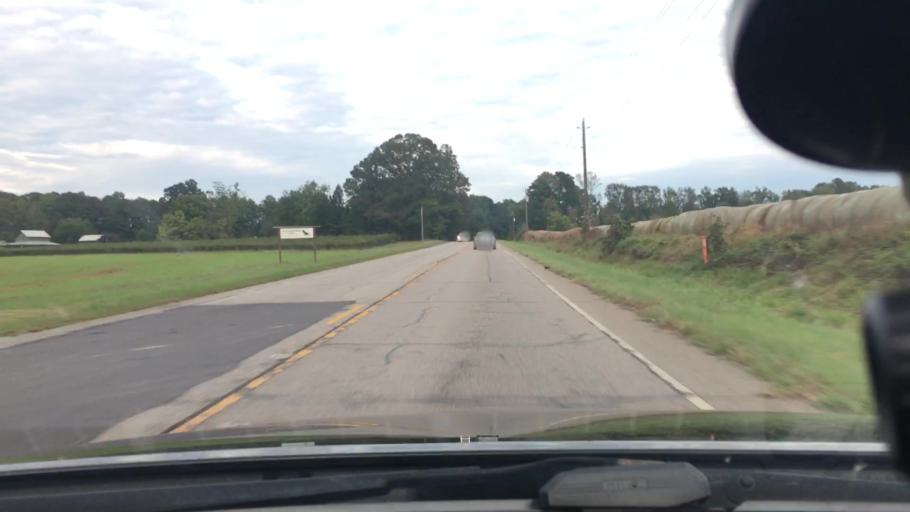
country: US
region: North Carolina
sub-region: Moore County
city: Carthage
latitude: 35.3540
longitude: -79.3475
